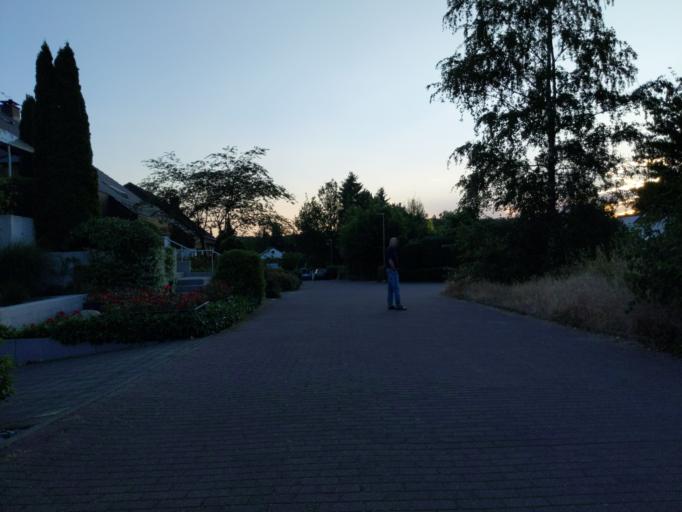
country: DE
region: North Rhine-Westphalia
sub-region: Regierungsbezirk Detmold
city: Bielefeld
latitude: 52.0235
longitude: 8.4869
